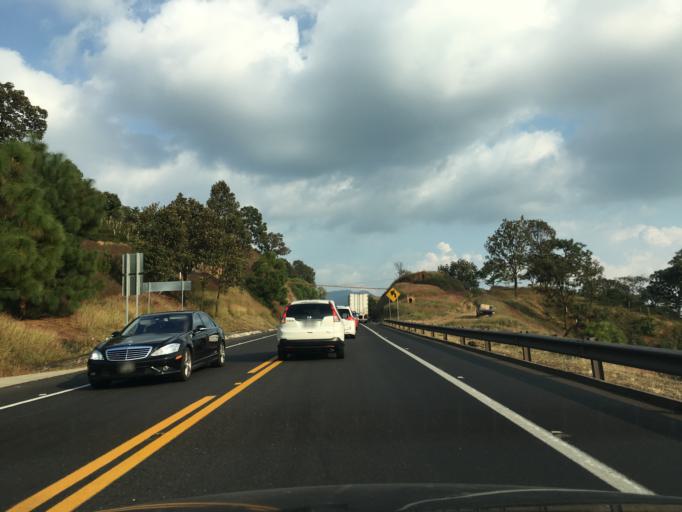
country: MX
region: Michoacan
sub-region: Ziracuaretiro
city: Patuan
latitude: 19.4329
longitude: -101.8990
